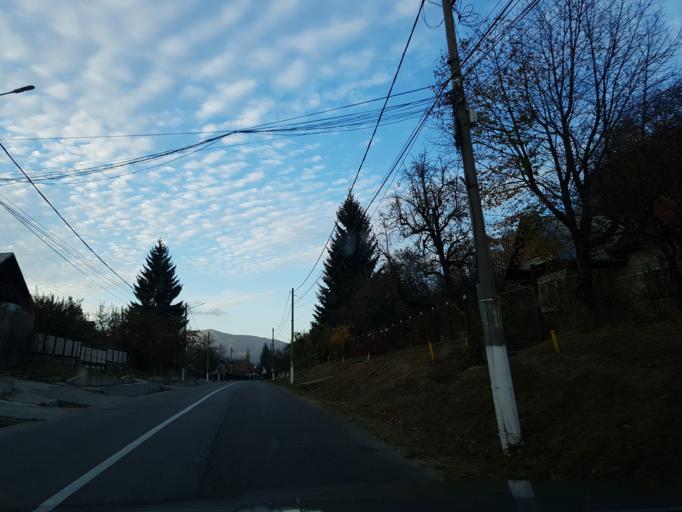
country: RO
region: Prahova
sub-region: Oras Breaza
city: Gura Beliei
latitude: 45.2119
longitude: 25.6457
